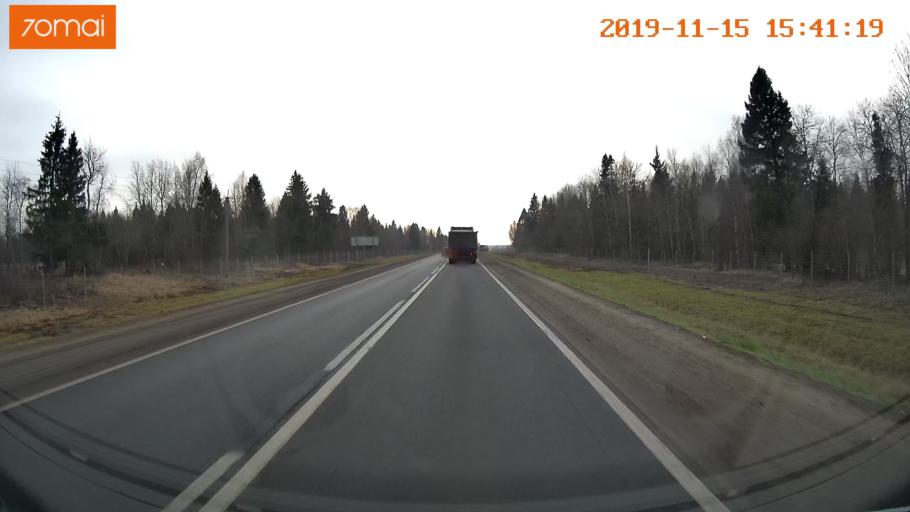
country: RU
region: Jaroslavl
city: Danilov
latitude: 58.0019
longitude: 40.0490
